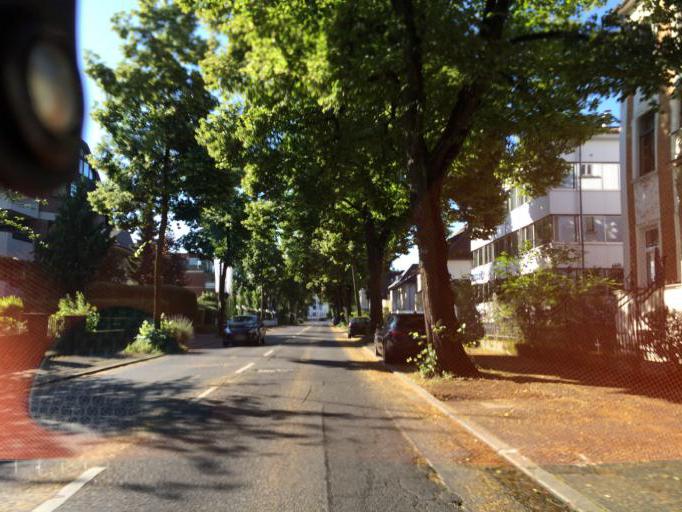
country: DE
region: North Rhine-Westphalia
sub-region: Regierungsbezirk Koln
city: Konigswinter
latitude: 50.6916
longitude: 7.1650
